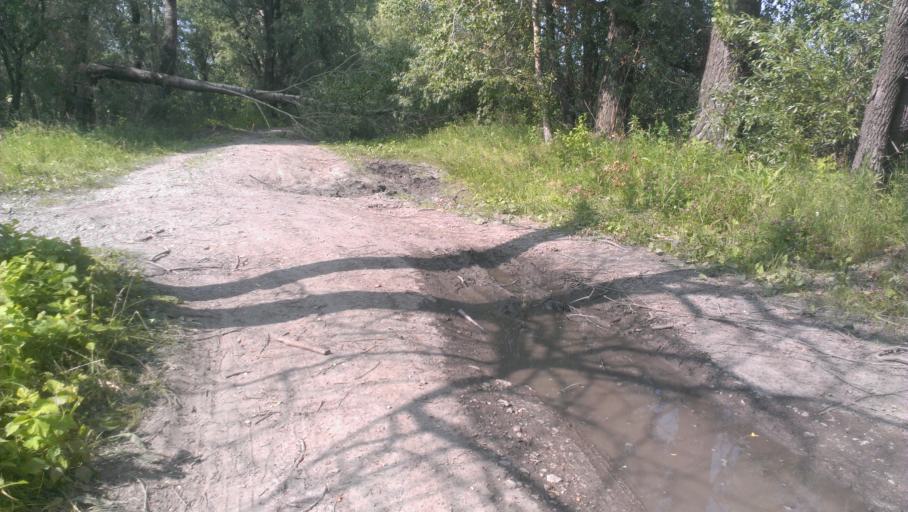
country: RU
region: Altai Krai
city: Novoaltaysk
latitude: 53.3755
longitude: 83.8570
